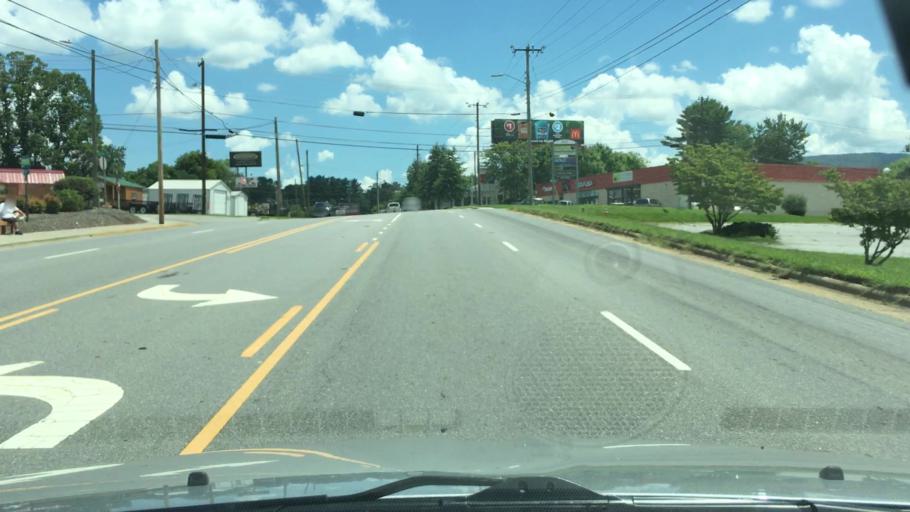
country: US
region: North Carolina
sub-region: Buncombe County
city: Asheville
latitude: 35.5866
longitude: -82.5075
